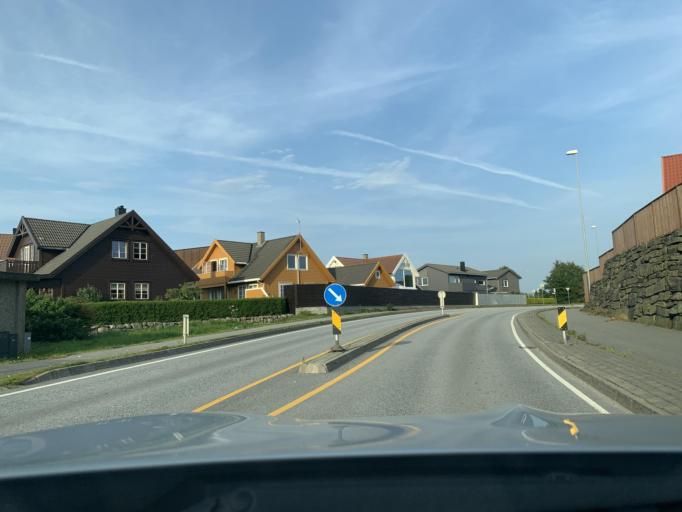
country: NO
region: Rogaland
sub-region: Time
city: Bryne
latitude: 58.7399
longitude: 5.6264
